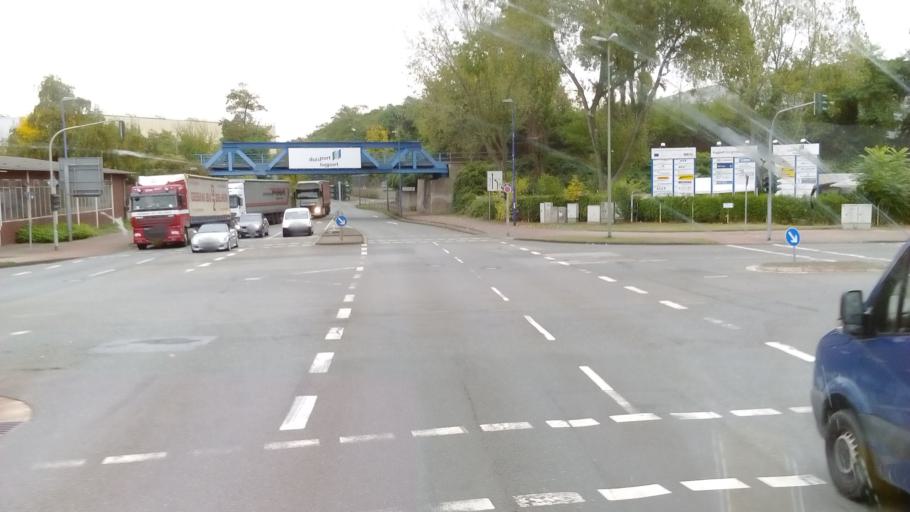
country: DE
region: North Rhine-Westphalia
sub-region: Regierungsbezirk Dusseldorf
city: Hochfeld
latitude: 51.3948
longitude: 6.7158
